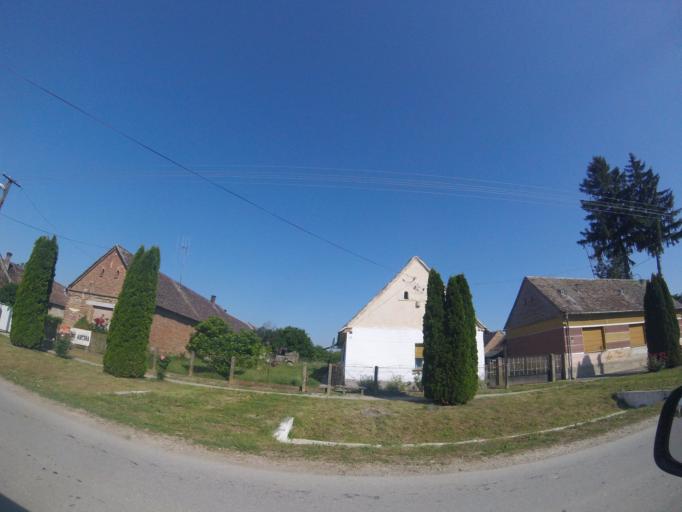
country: HU
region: Baranya
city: Sellye
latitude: 45.9247
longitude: 17.8738
